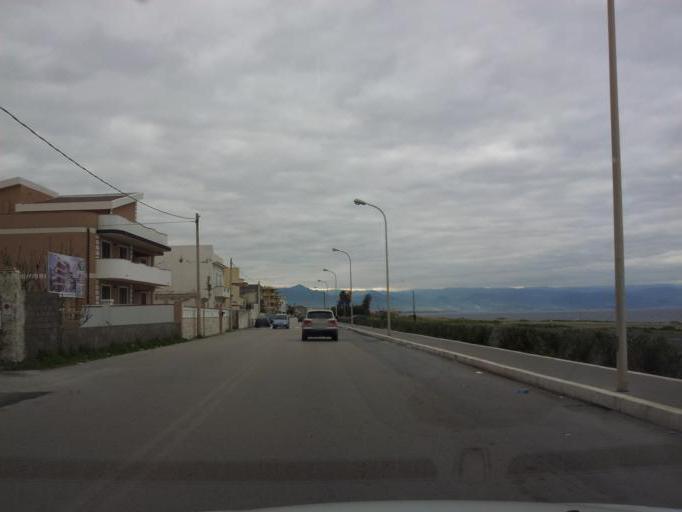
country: IT
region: Sicily
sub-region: Messina
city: Milazzo
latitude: 38.2186
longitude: 15.2330
